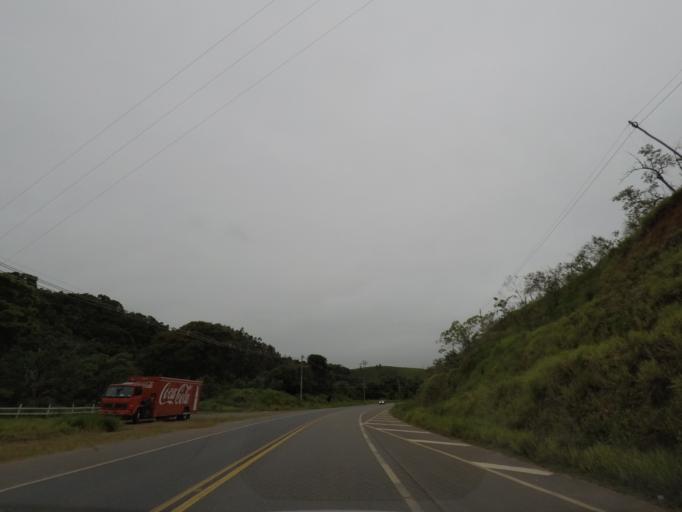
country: BR
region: Sao Paulo
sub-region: Cunha
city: Cunha
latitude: -23.0582
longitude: -44.9901
